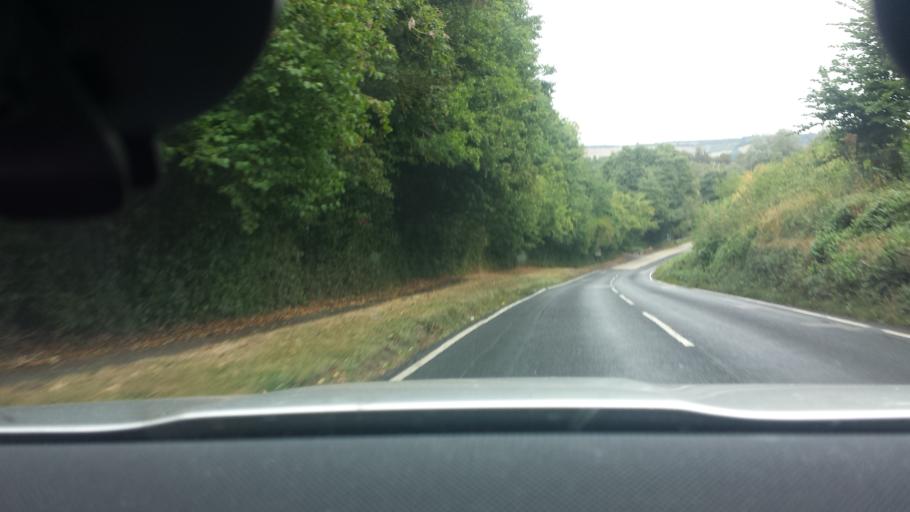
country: GB
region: England
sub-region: Kent
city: Harrietsham
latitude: 51.2534
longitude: 0.6186
